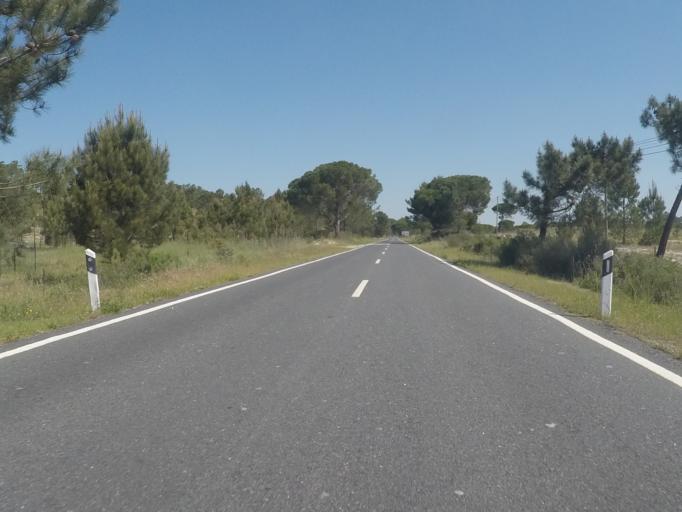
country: PT
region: Setubal
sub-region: Grandola
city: Grandola
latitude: 38.2907
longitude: -8.7265
